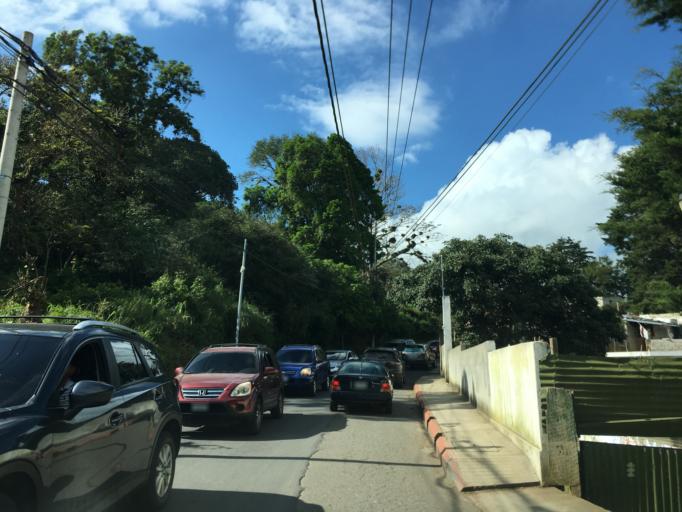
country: GT
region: Guatemala
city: San Jose Pinula
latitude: 14.5640
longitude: -90.4375
